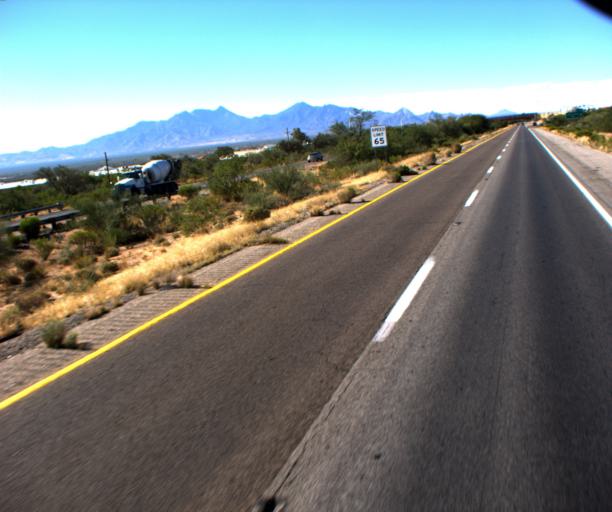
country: US
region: Arizona
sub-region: Pima County
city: Sahuarita
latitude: 31.9127
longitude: -110.9860
